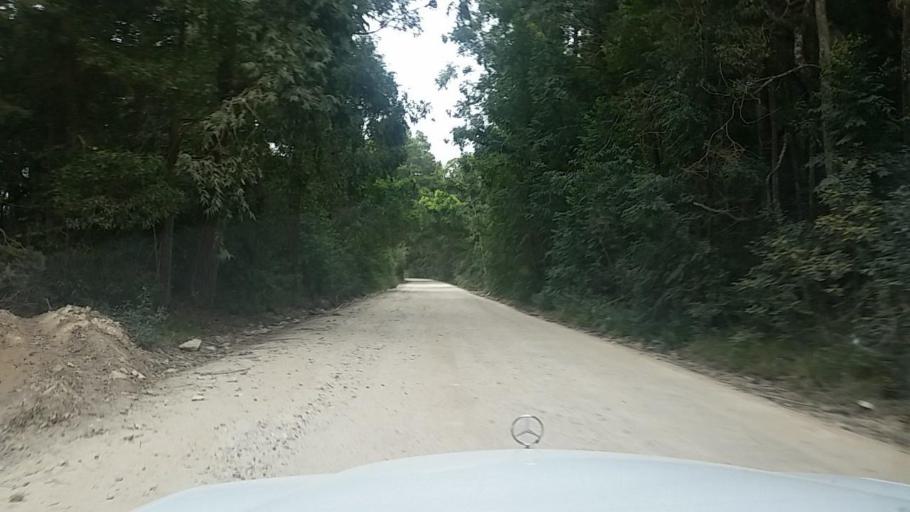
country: ZA
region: Western Cape
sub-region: Eden District Municipality
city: Knysna
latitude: -33.9771
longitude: 23.1396
